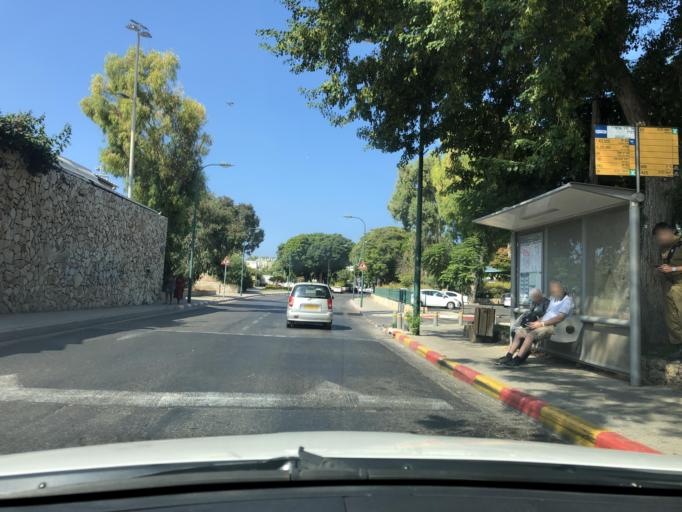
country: IL
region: Tel Aviv
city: Yafo
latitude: 32.0373
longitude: 34.7576
